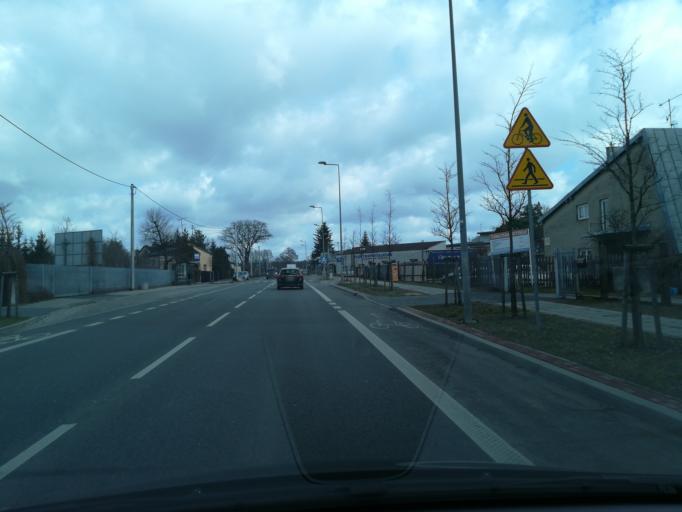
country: PL
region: Silesian Voivodeship
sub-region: Czestochowa
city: Czestochowa
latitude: 50.8262
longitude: 19.1357
